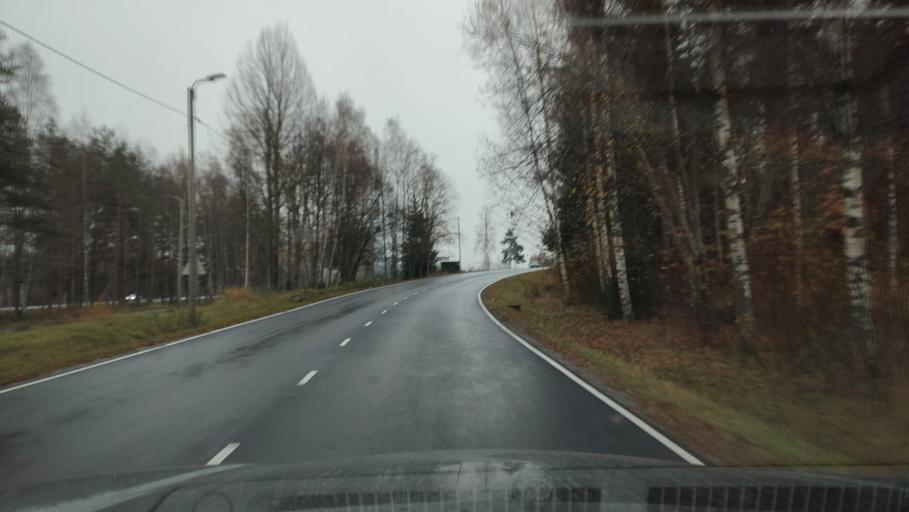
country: FI
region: Ostrobothnia
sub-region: Vaasa
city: Vaasa
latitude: 63.0979
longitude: 21.6500
